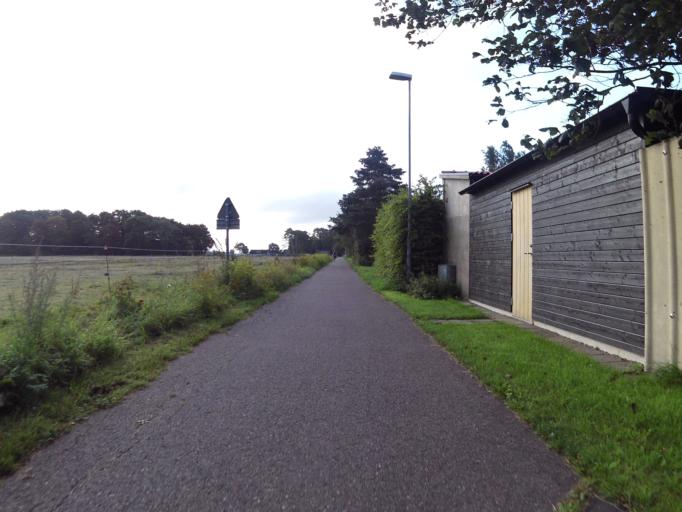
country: SE
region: Skane
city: Bjarred
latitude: 55.7014
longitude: 13.0459
